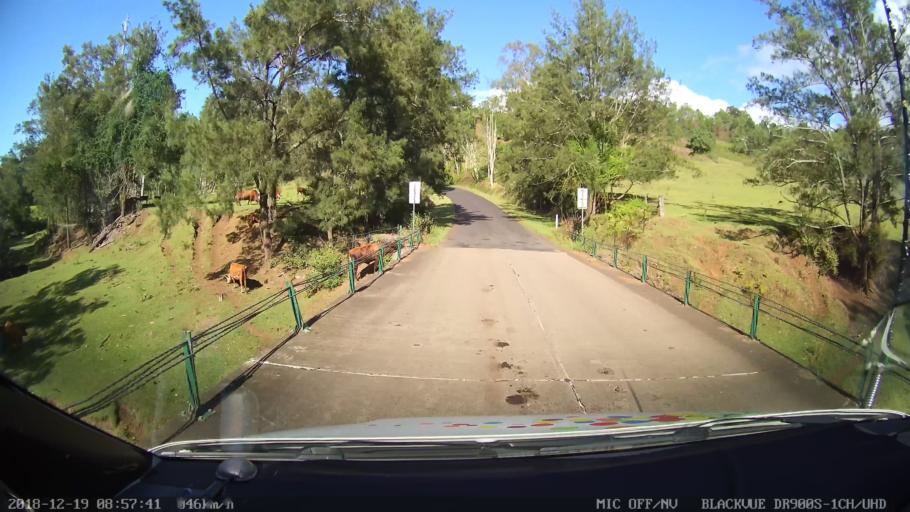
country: AU
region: New South Wales
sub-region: Kyogle
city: Kyogle
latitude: -28.4213
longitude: 152.9700
